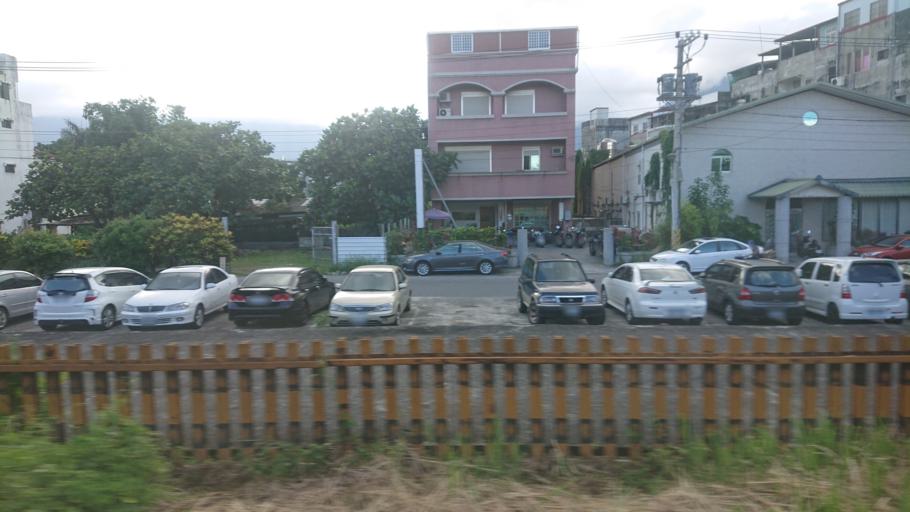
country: TW
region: Taiwan
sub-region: Hualien
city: Hualian
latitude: 23.9842
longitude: 121.5966
